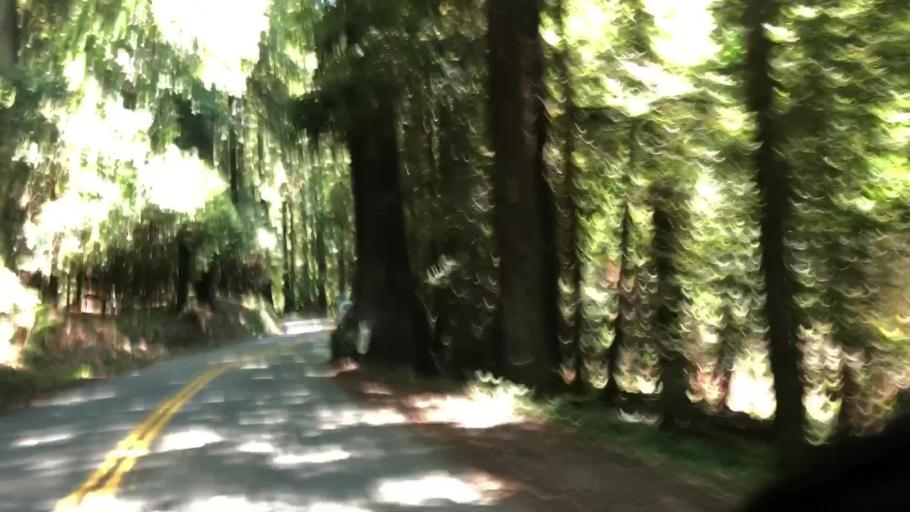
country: US
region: California
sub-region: Santa Cruz County
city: Corralitos
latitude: 37.0220
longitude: -121.8198
